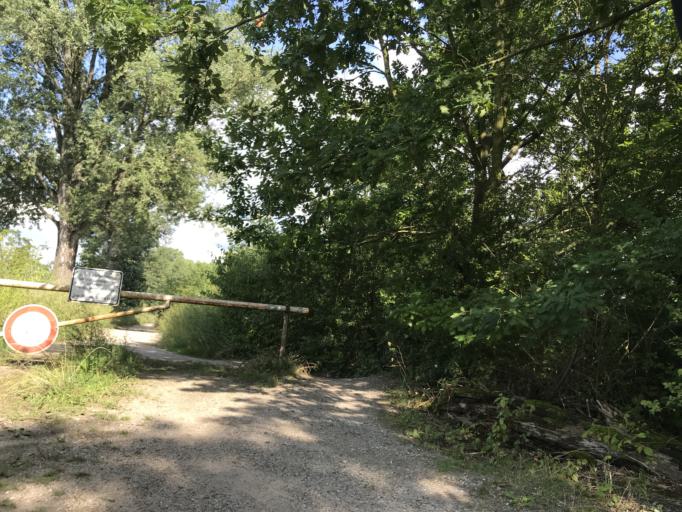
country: DE
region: Rheinland-Pfalz
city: Bobenheim-Roxheim
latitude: 49.5855
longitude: 8.3862
